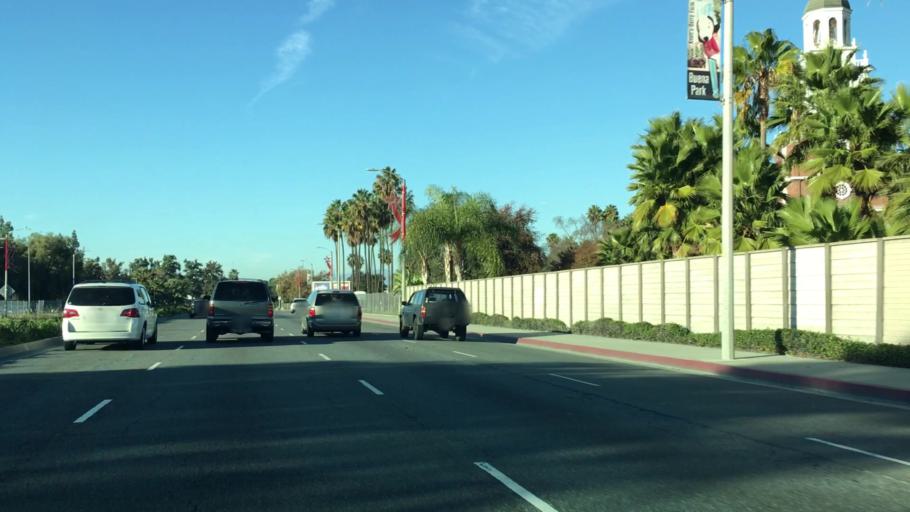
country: US
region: California
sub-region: Orange County
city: Buena Park
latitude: 33.8411
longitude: -117.9962
